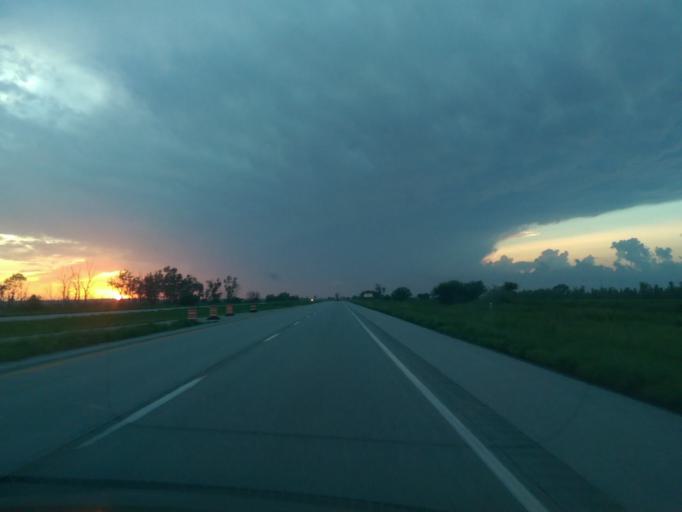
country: US
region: Iowa
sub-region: Fremont County
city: Hamburg
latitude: 40.6179
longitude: -95.6986
